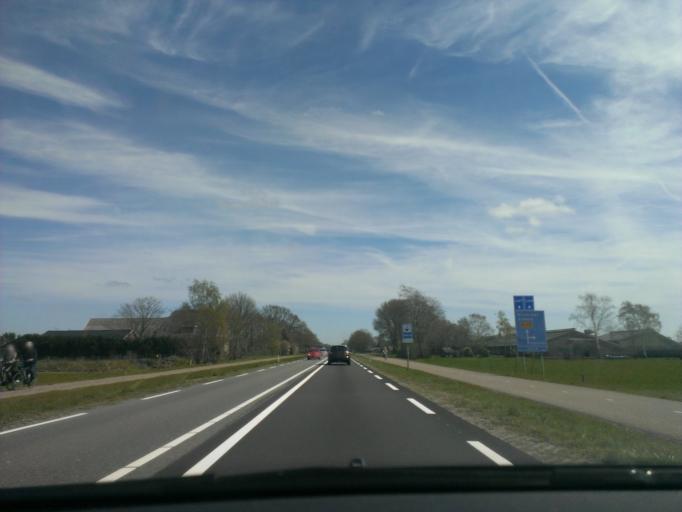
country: NL
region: Overijssel
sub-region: Gemeente Raalte
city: Raalte
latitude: 52.3711
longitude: 6.3702
